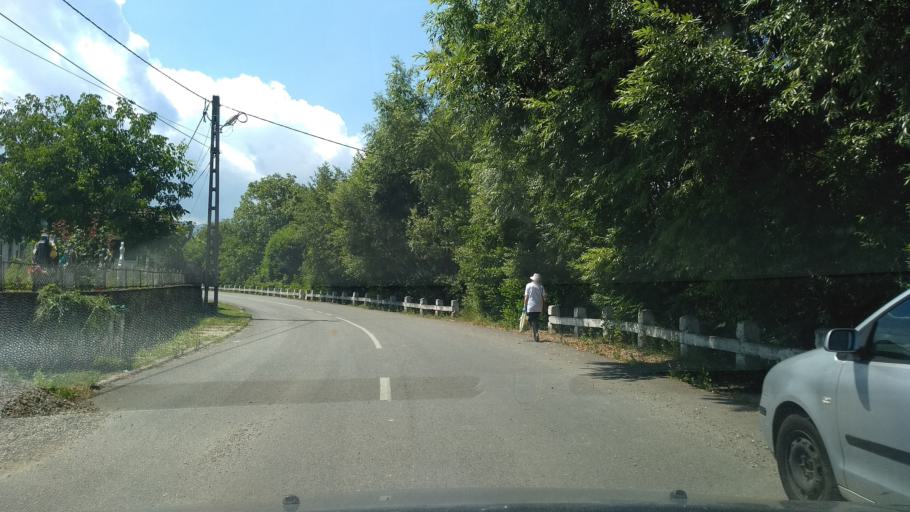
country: RO
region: Hunedoara
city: Salasu de Sus
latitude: 45.5093
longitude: 22.9538
